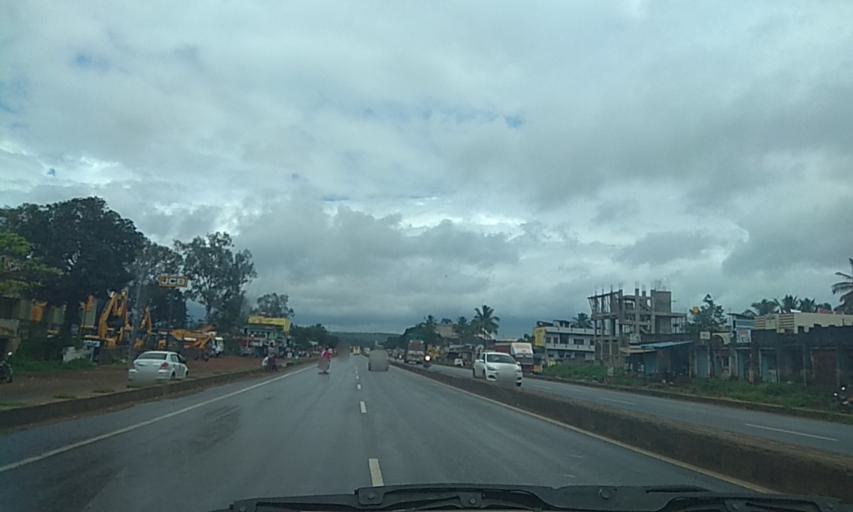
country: IN
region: Karnataka
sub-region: Belgaum
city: Belgaum
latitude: 15.9355
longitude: 74.5261
